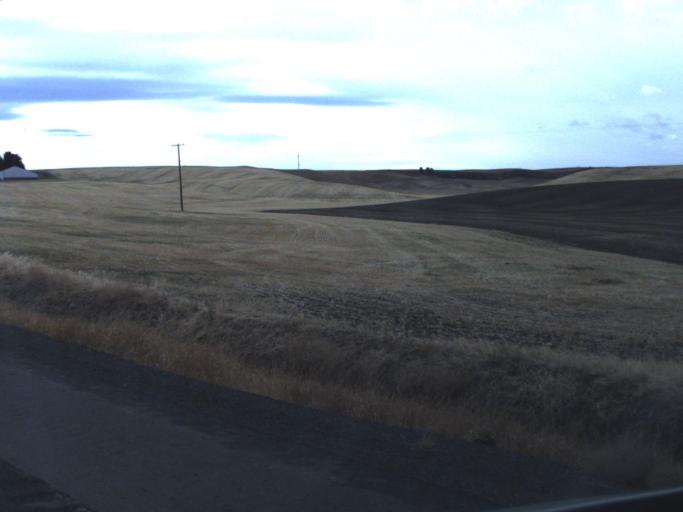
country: US
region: Washington
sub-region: Asotin County
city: Clarkston
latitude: 46.5049
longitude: -117.0787
